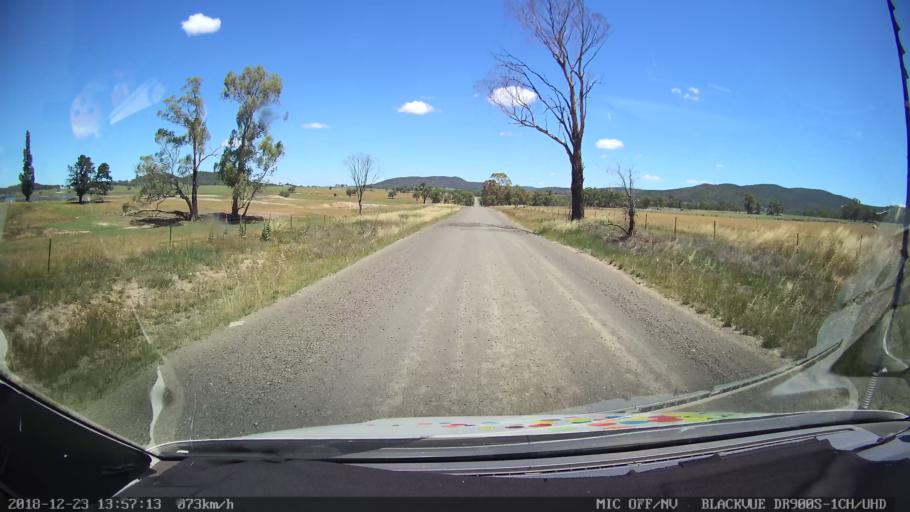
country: AU
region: New South Wales
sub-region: Tamworth Municipality
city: Manilla
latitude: -30.5857
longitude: 151.0941
